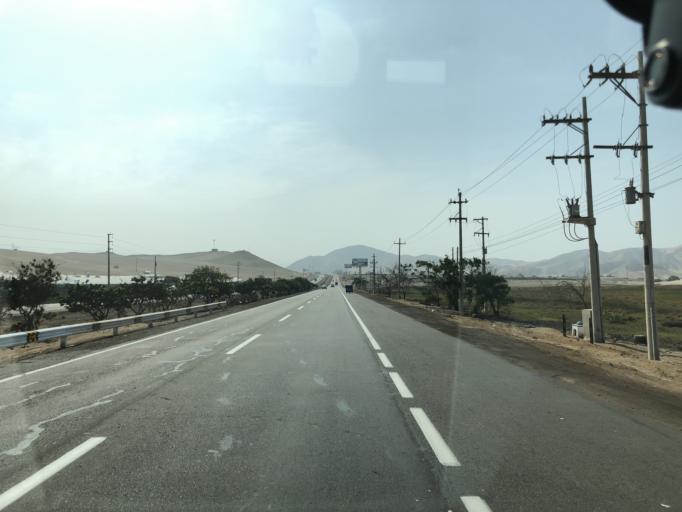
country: PE
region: Lima
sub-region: Provincia de Canete
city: Chilca
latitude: -12.5663
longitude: -76.7013
